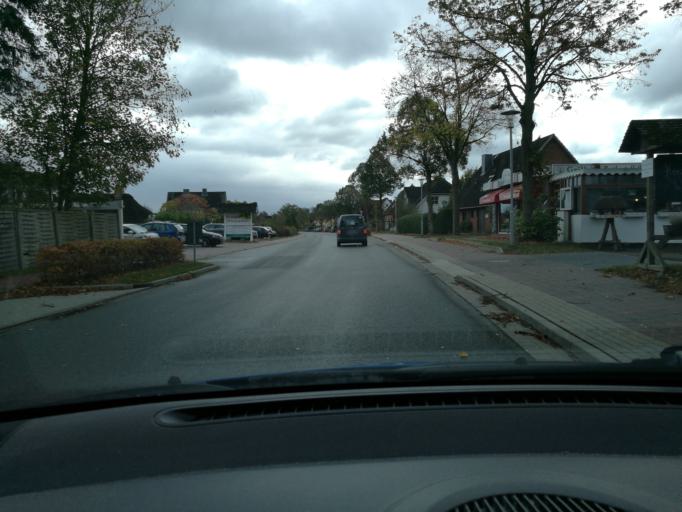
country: DE
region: Schleswig-Holstein
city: Pogeez
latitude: 53.7534
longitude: 10.7284
